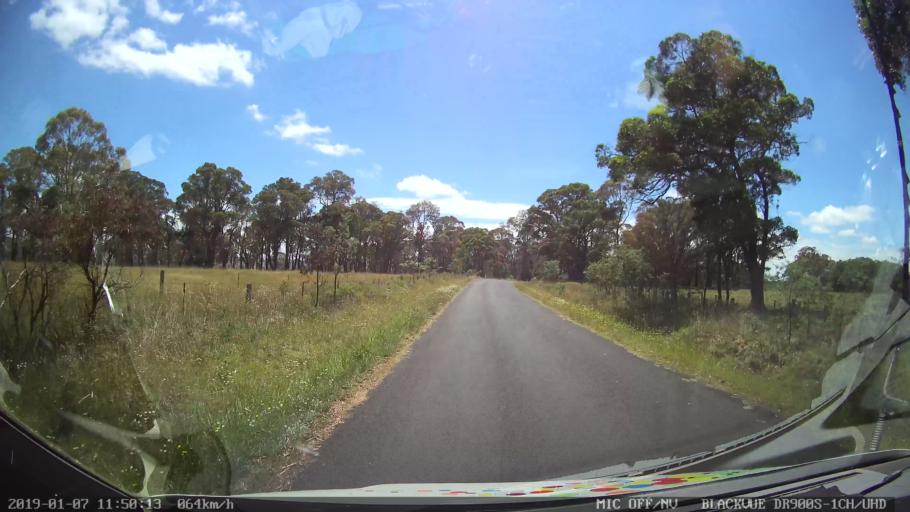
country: AU
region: New South Wales
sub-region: Guyra
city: Guyra
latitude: -30.3132
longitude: 151.6337
